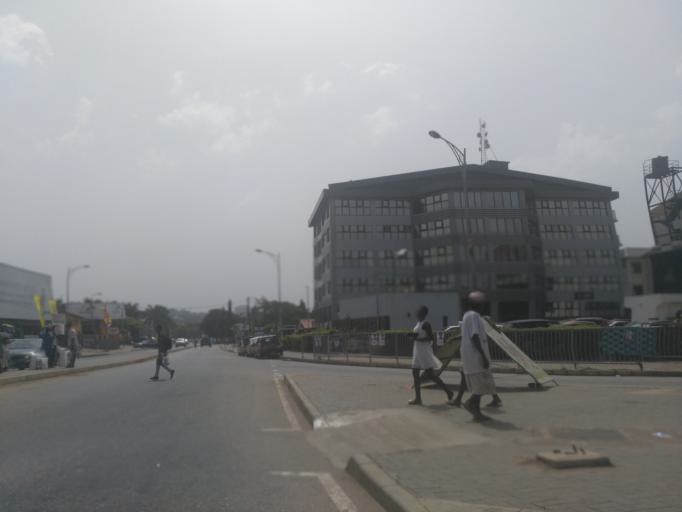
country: GH
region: Greater Accra
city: Dome
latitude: 5.6178
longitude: -0.1926
